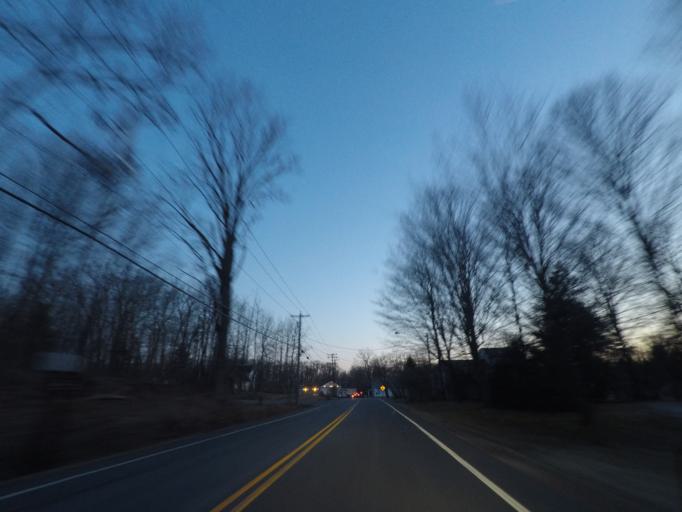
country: US
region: New York
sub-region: Schenectady County
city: Niskayuna
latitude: 42.7986
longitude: -73.8276
